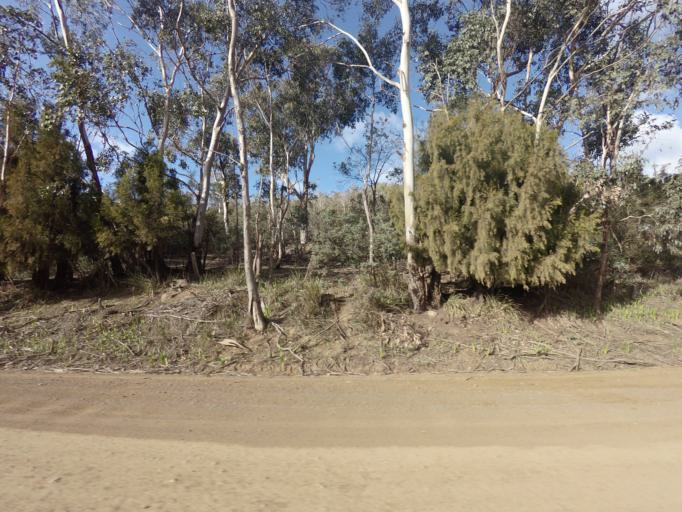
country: AU
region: Tasmania
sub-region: Derwent Valley
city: New Norfolk
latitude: -42.8107
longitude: 147.1317
